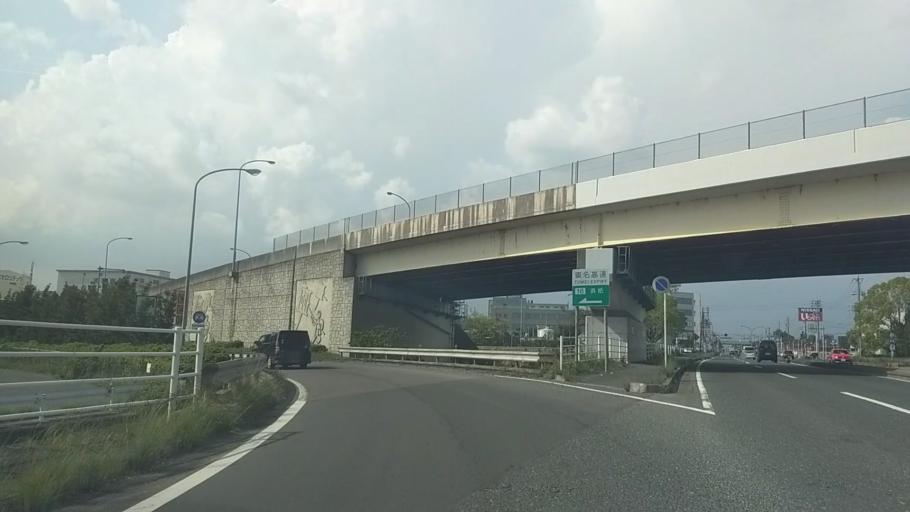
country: JP
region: Shizuoka
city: Hamakita
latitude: 34.7426
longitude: 137.7902
